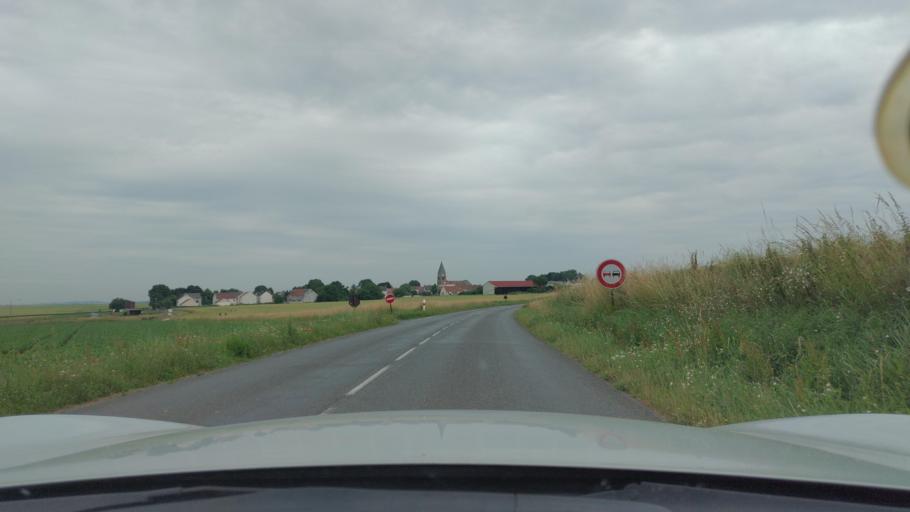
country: FR
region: Ile-de-France
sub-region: Departement de Seine-et-Marne
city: Cregy-les-Meaux
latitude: 49.0124
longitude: 2.8798
